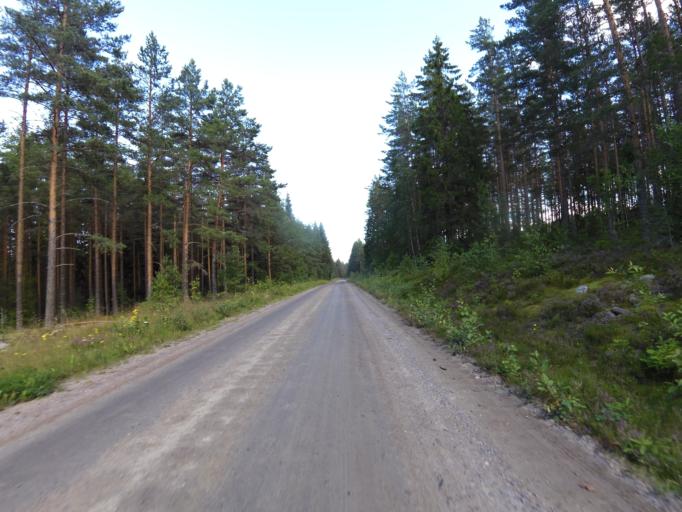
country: SE
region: Gaevleborg
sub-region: Hofors Kommun
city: Hofors
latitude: 60.5067
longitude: 16.3821
